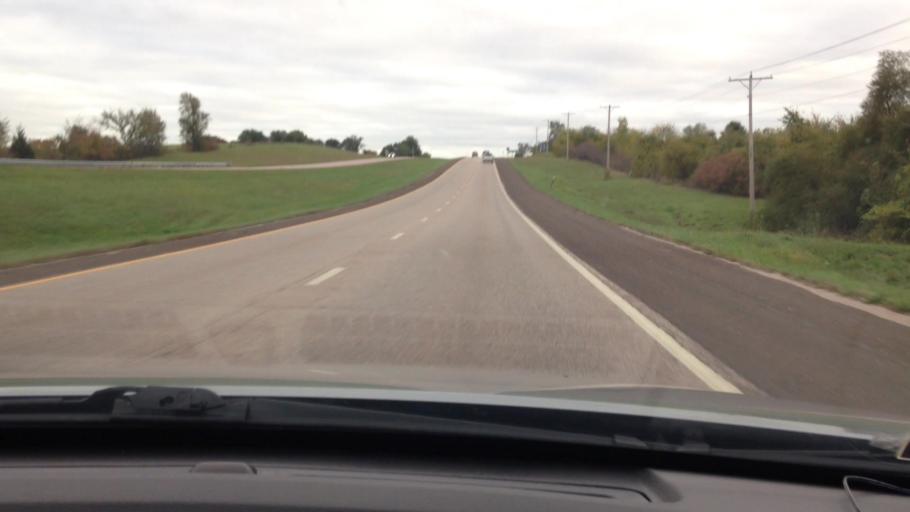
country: US
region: Kansas
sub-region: Leavenworth County
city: Basehor
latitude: 39.1644
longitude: -94.9008
